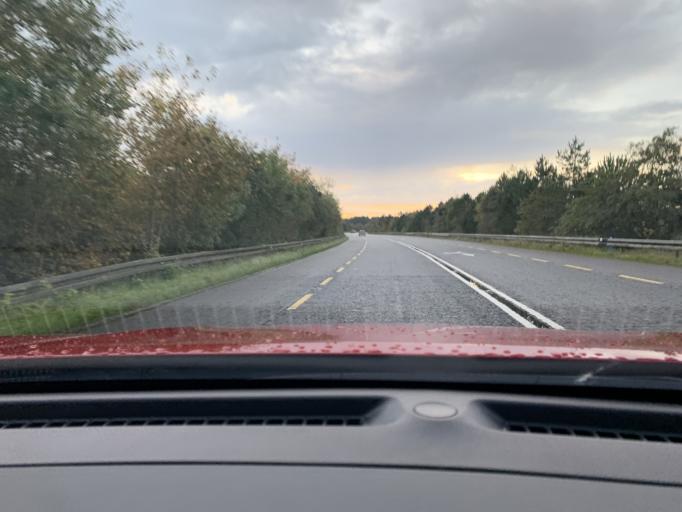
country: IE
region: Connaught
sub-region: County Leitrim
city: Carrick-on-Shannon
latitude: 53.9490
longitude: -8.1335
